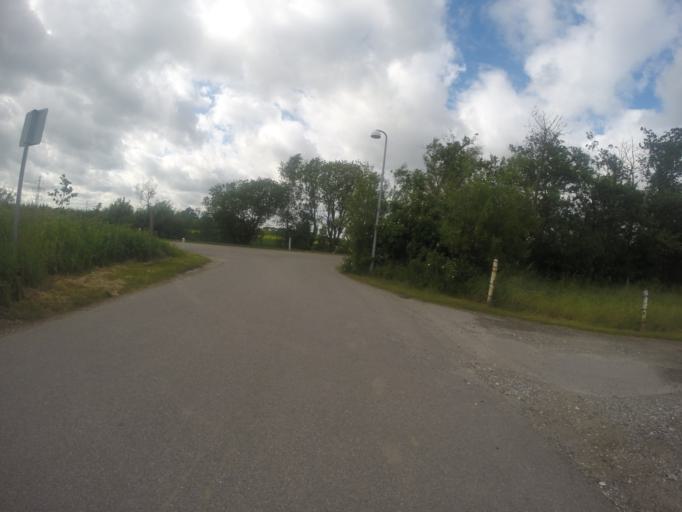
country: DK
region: Capital Region
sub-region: Hoje-Taastrup Kommune
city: Taastrup
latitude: 55.6723
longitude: 12.2976
